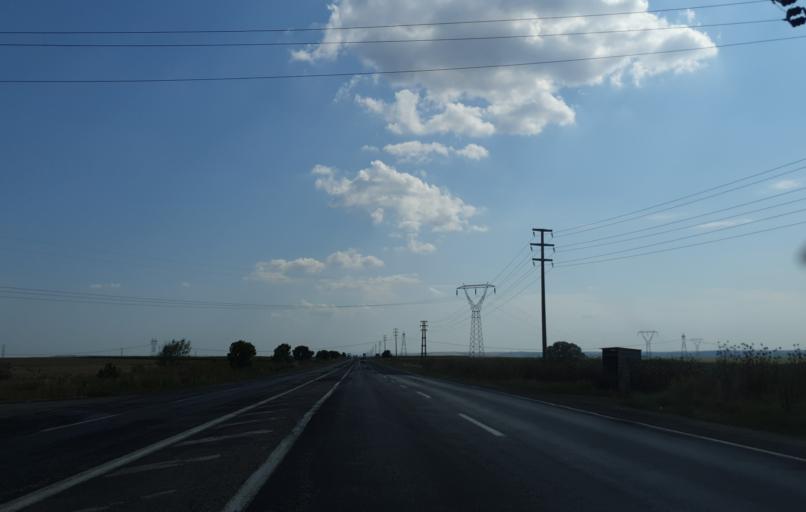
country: TR
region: Kirklareli
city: Buyukkaristiran
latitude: 41.2422
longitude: 27.5382
